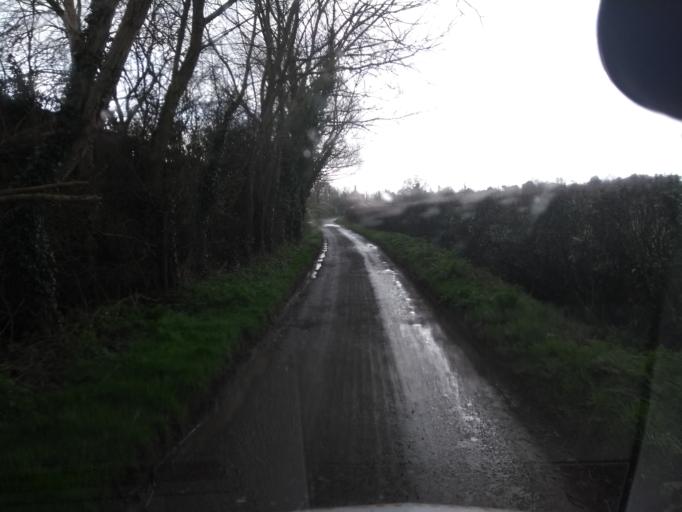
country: GB
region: England
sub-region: Somerset
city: South Petherton
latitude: 50.9726
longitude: -2.8112
